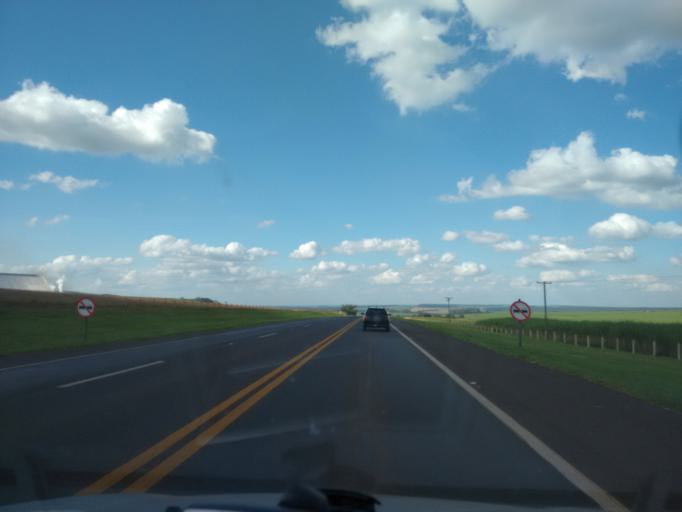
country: BR
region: Sao Paulo
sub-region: Americo Brasiliense
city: Americo Brasiliense
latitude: -21.7655
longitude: -48.0843
